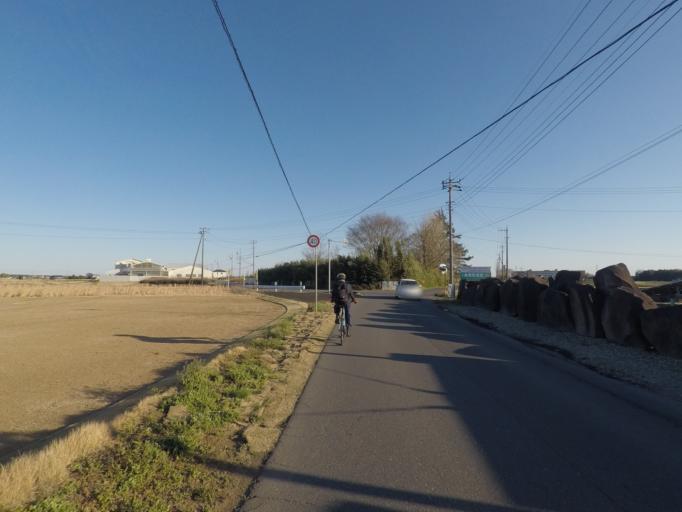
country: JP
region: Ibaraki
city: Ishige
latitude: 36.1338
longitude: 140.0188
